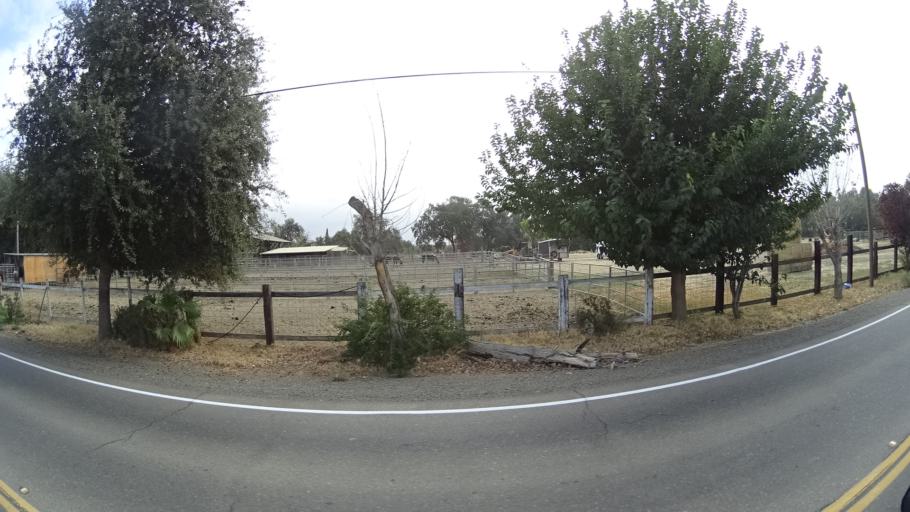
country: US
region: California
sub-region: Yolo County
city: Esparto
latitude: 38.6952
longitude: -122.0385
